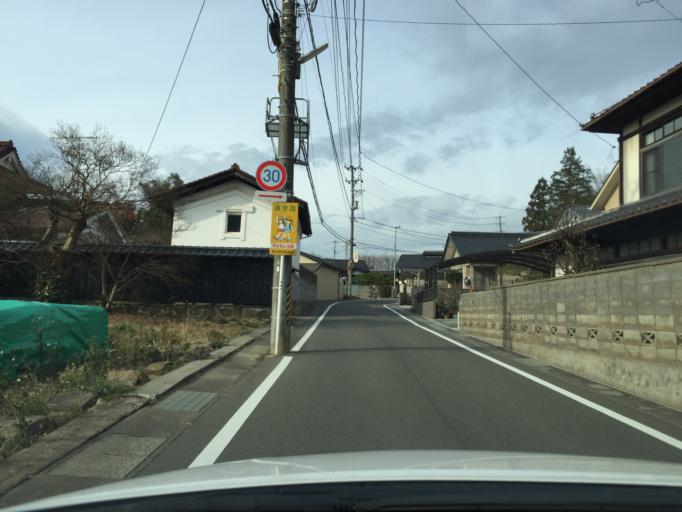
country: JP
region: Fukushima
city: Fukushima-shi
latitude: 37.7028
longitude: 140.4646
